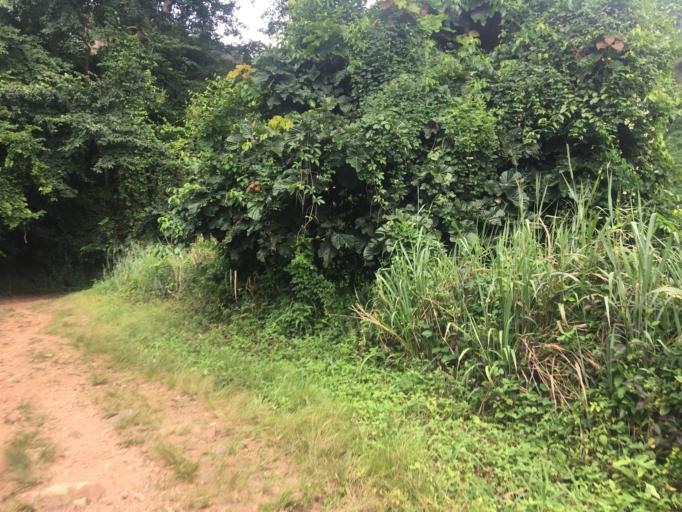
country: TG
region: Plateaux
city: Kpalime
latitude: 7.0062
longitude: 0.6468
